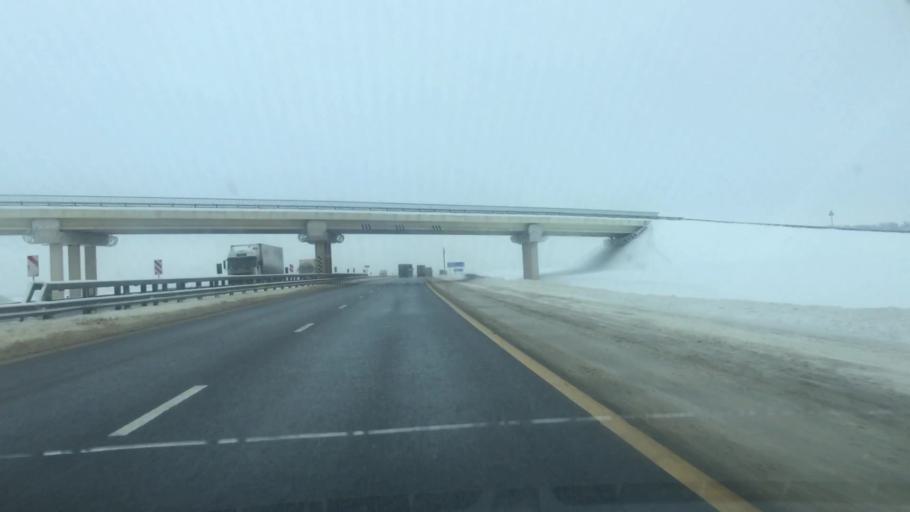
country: RU
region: Lipetsk
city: Stanovoye
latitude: 52.7440
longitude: 38.4703
